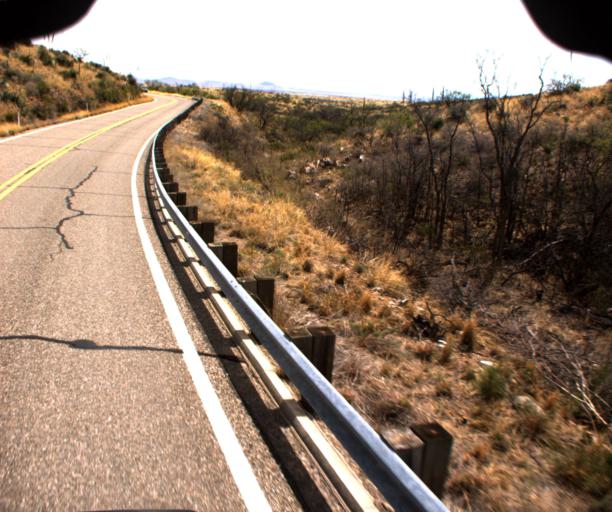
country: US
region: Arizona
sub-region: Cochise County
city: Willcox
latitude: 32.1515
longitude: -109.5648
